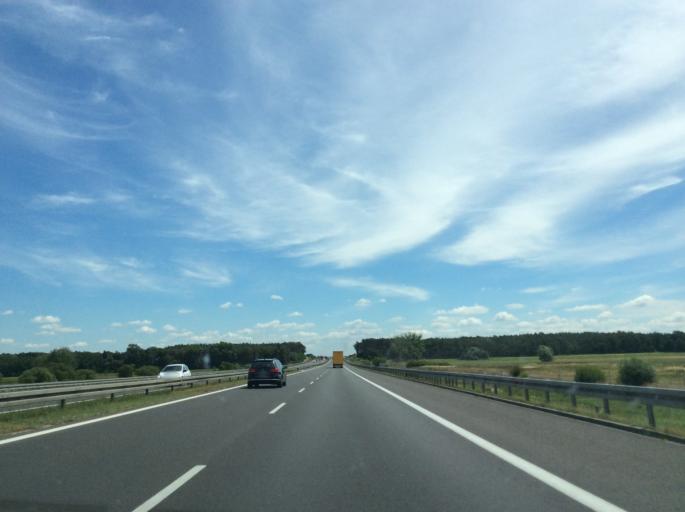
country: PL
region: Greater Poland Voivodeship
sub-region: Powiat poznanski
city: Swarzedz
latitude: 52.3404
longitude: 17.0372
